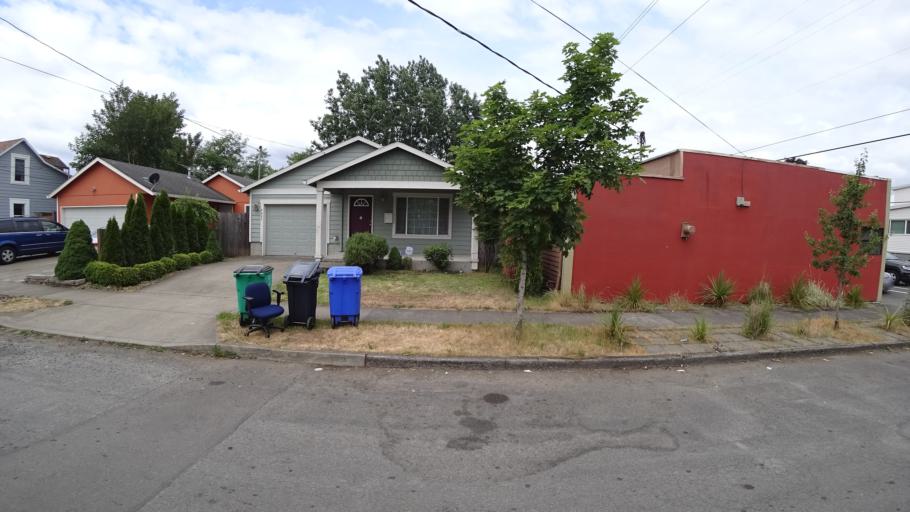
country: US
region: Oregon
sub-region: Multnomah County
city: Lents
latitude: 45.4791
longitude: -122.5725
